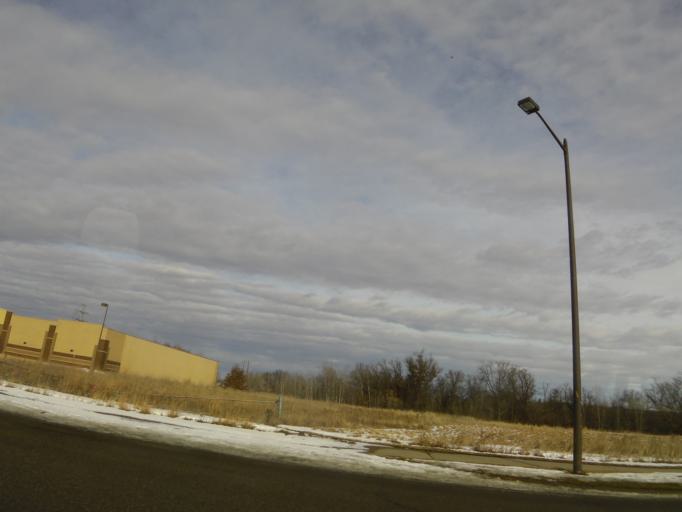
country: US
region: Minnesota
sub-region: Dakota County
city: Lakeville
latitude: 44.6832
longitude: -93.2857
